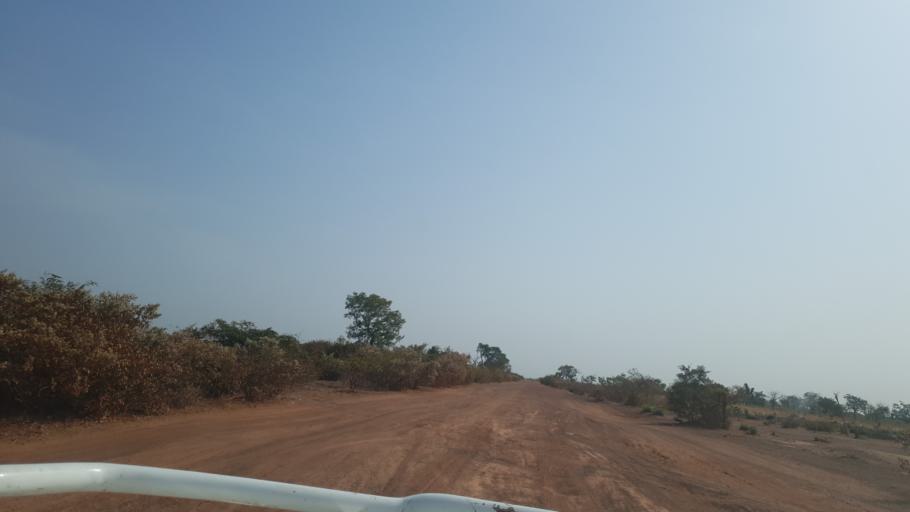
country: ML
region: Koulikoro
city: Dioila
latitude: 12.6698
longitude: -6.6587
